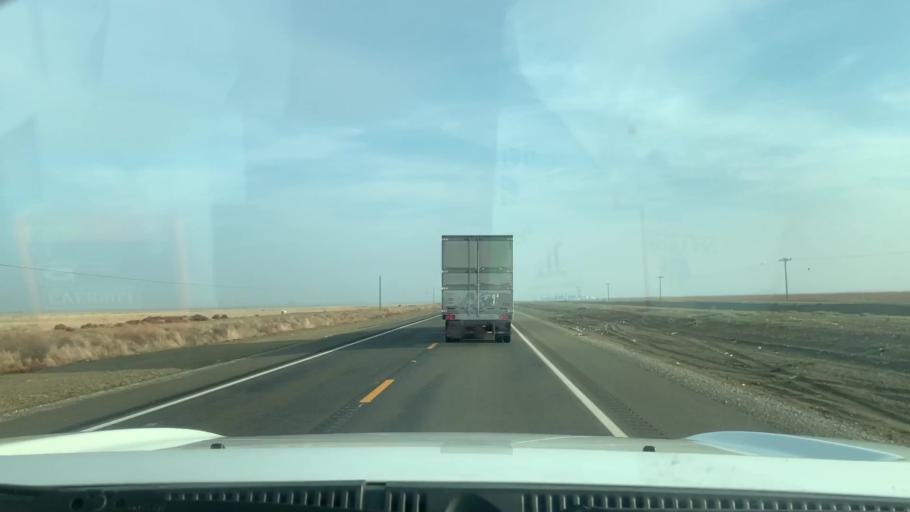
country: US
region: California
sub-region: Kings County
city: Stratford
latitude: 36.1411
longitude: -119.8749
